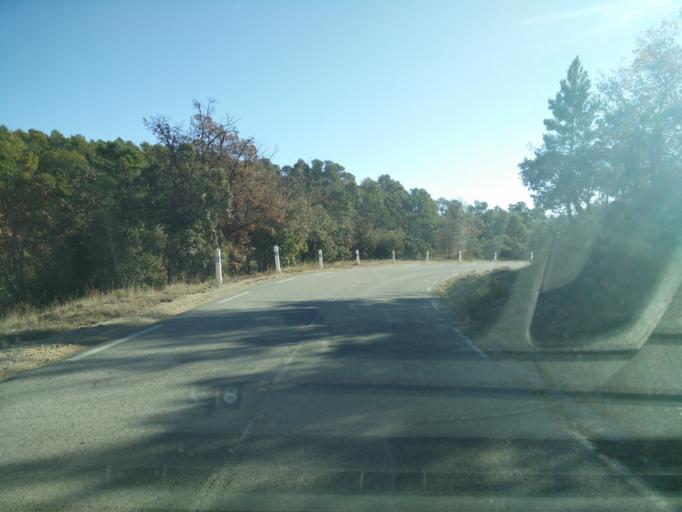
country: FR
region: Provence-Alpes-Cote d'Azur
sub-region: Departement du Var
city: Salernes
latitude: 43.5923
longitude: 6.2238
